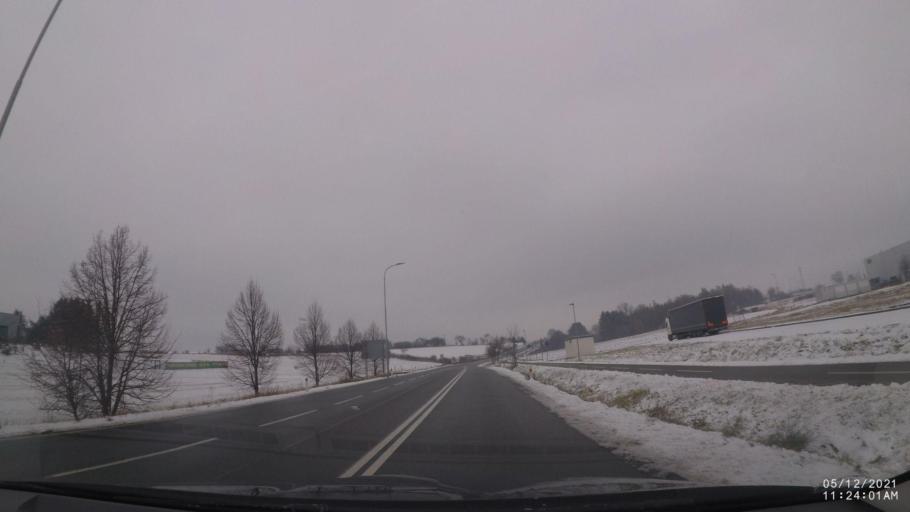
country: CZ
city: Solnice
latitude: 50.1959
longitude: 16.2482
